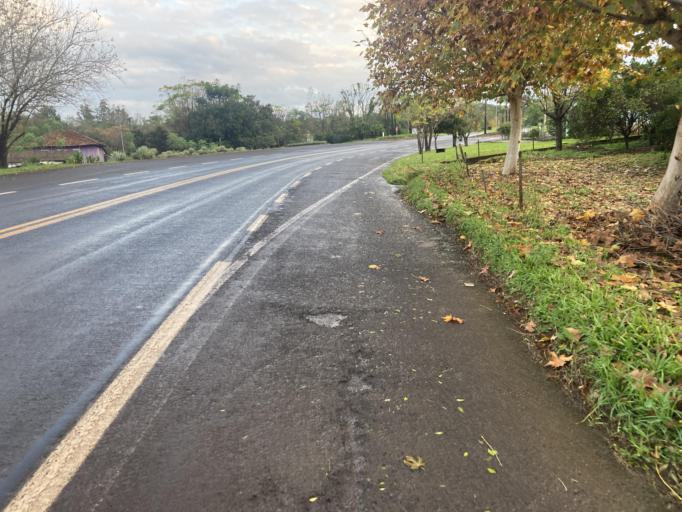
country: BR
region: Rio Grande do Sul
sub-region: Sao Pedro Do Butia
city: Butia Inferior
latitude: -27.9919
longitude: -54.8326
